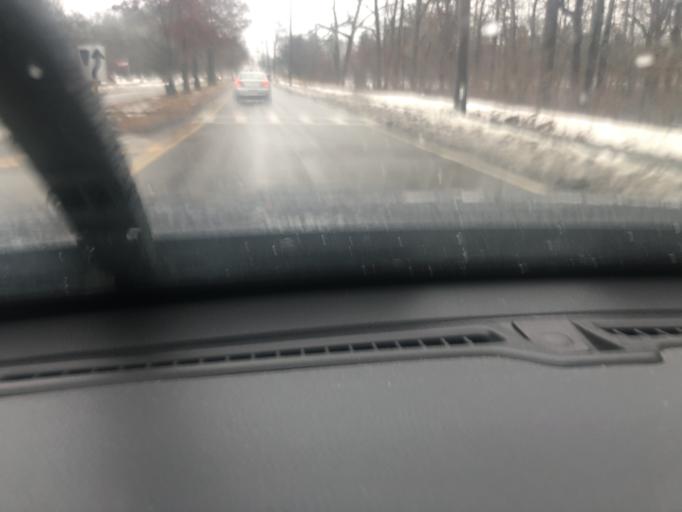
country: US
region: Massachusetts
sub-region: Norfolk County
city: Avon
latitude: 42.1015
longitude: -71.0446
